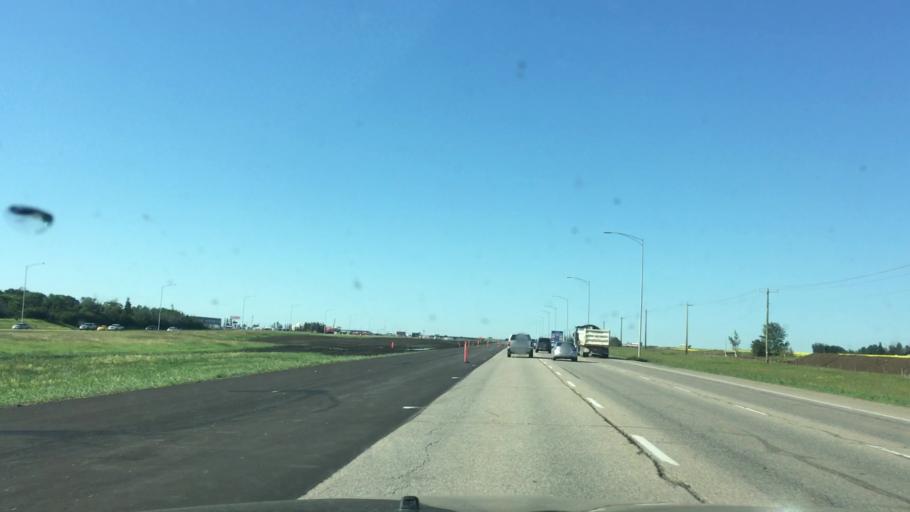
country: CA
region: Alberta
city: Leduc
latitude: 53.3565
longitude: -113.5385
